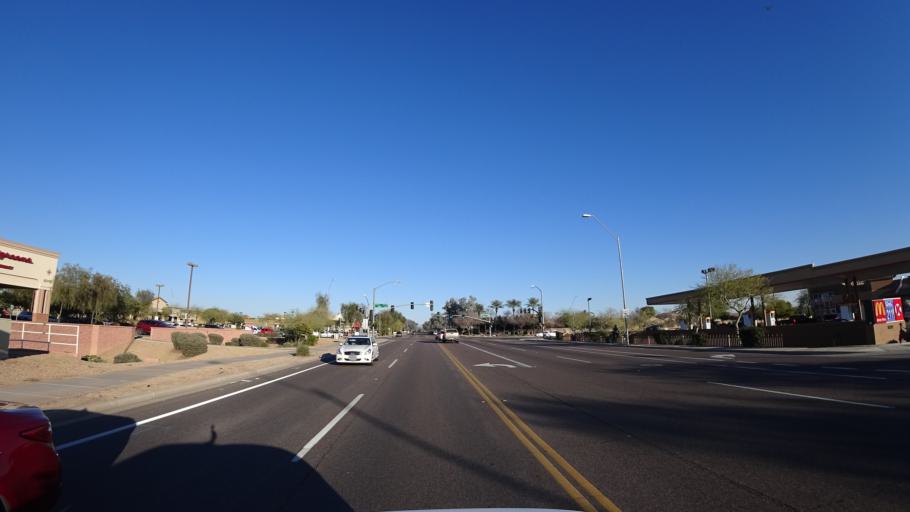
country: US
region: Arizona
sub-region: Maricopa County
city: Sun City
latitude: 33.6816
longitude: -112.2387
